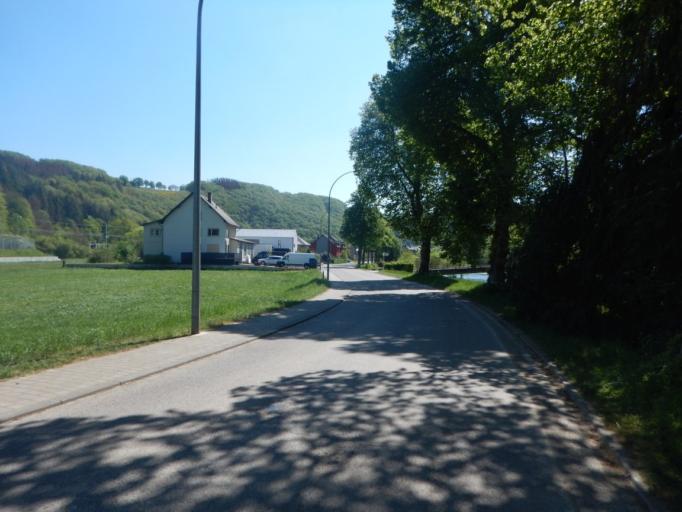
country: LU
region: Diekirch
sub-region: Canton de Diekirch
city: Bourscheid
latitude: 49.8962
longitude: 6.0907
